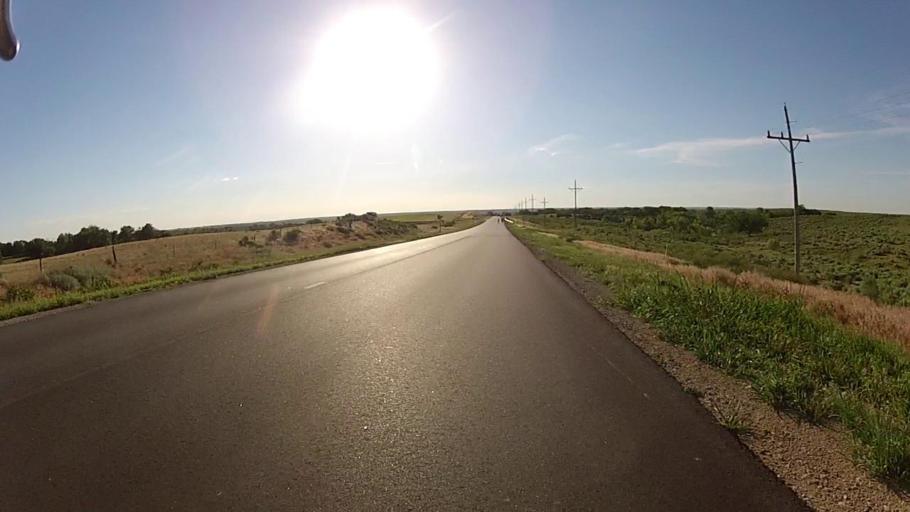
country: US
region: Kansas
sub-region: Comanche County
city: Coldwater
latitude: 37.2820
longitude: -99.0903
